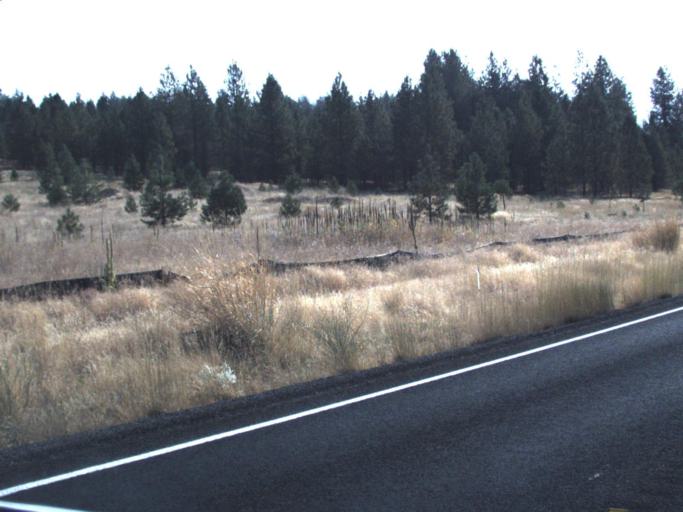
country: US
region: Washington
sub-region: Spokane County
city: Deer Park
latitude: 47.8251
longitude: -117.5930
